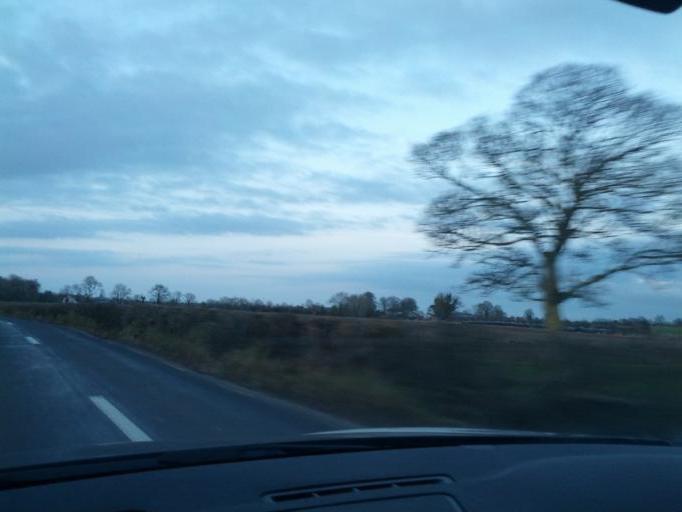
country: IE
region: Connaught
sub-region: County Galway
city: Portumna
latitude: 53.0359
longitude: -8.1162
